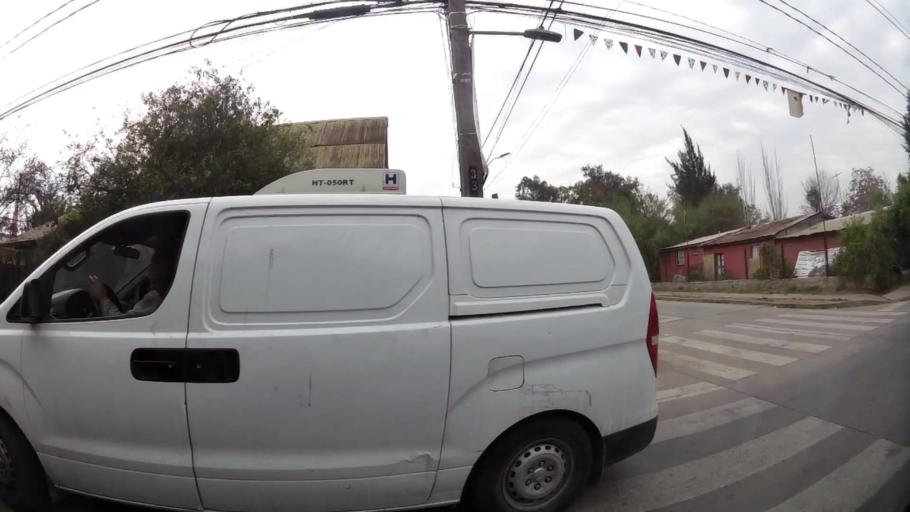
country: CL
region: Santiago Metropolitan
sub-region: Provincia de Chacabuco
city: Lampa
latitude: -33.2353
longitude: -70.8067
